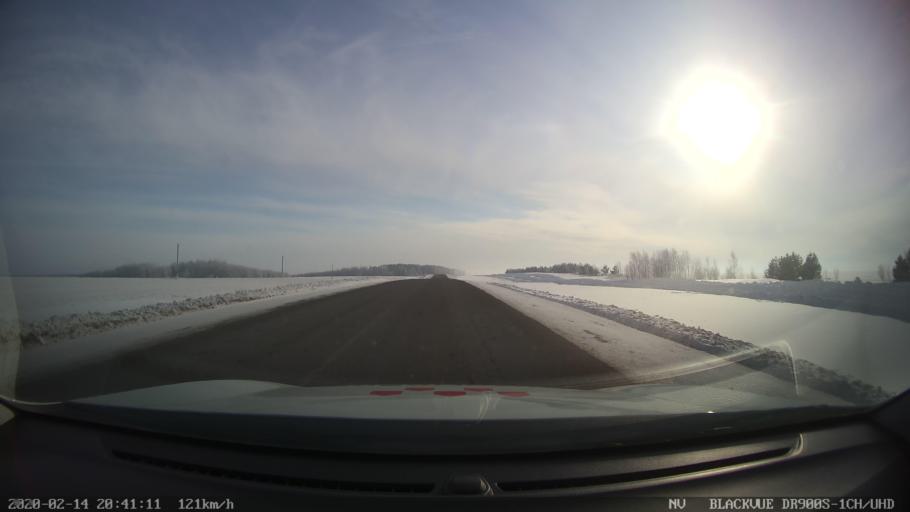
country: RU
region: Tatarstan
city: Kuybyshevskiy Zaton
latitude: 55.3329
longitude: 49.1127
